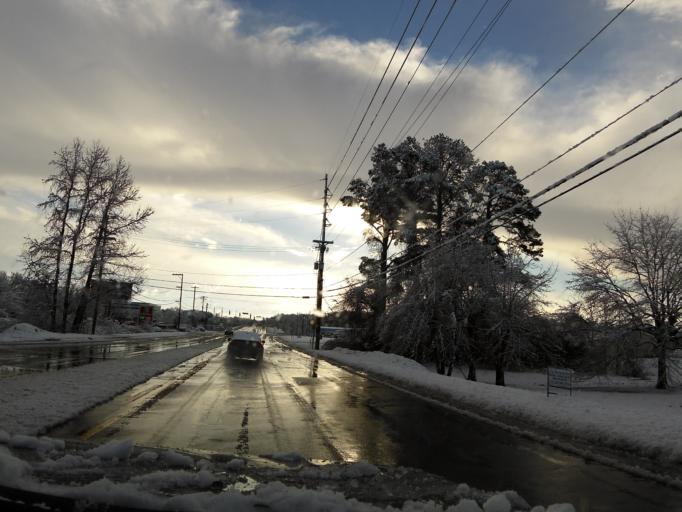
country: US
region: North Carolina
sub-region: Nash County
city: Rocky Mount
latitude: 35.9361
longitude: -77.8334
